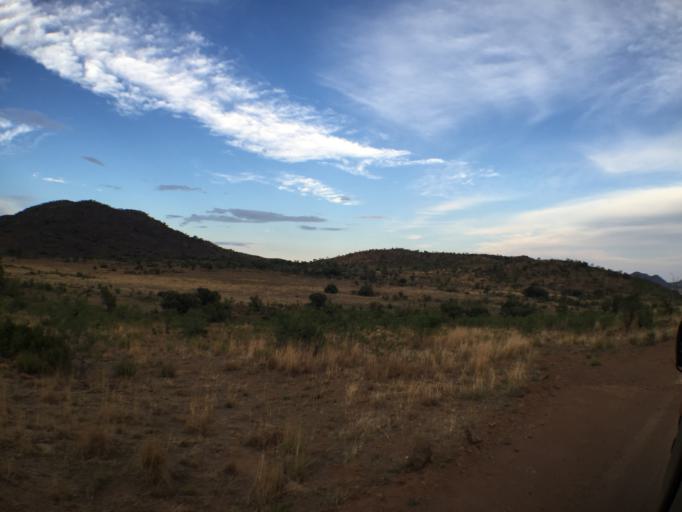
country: ZA
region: North-West
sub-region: Bojanala Platinum District Municipality
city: Mogwase
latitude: -25.2251
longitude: 27.0790
